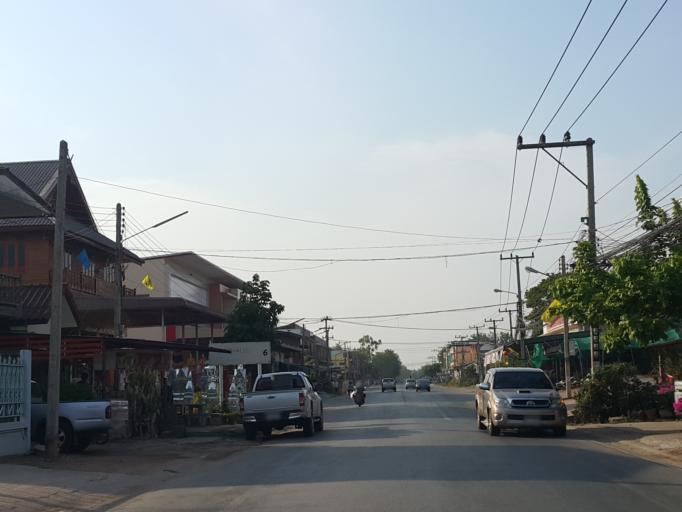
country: TH
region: Phitsanulok
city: Phrom Phiram
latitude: 17.1039
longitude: 100.1651
